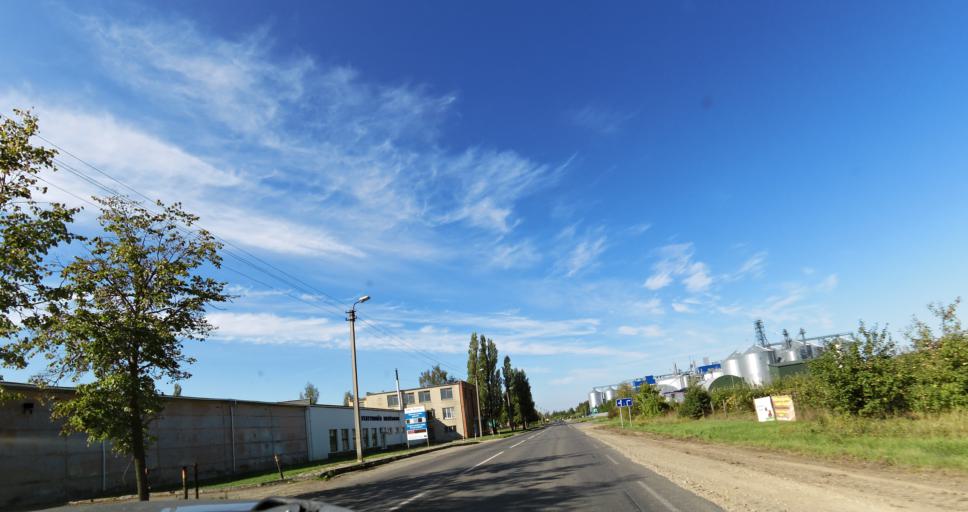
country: LT
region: Panevezys
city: Pasvalys
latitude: 56.0705
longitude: 24.4140
